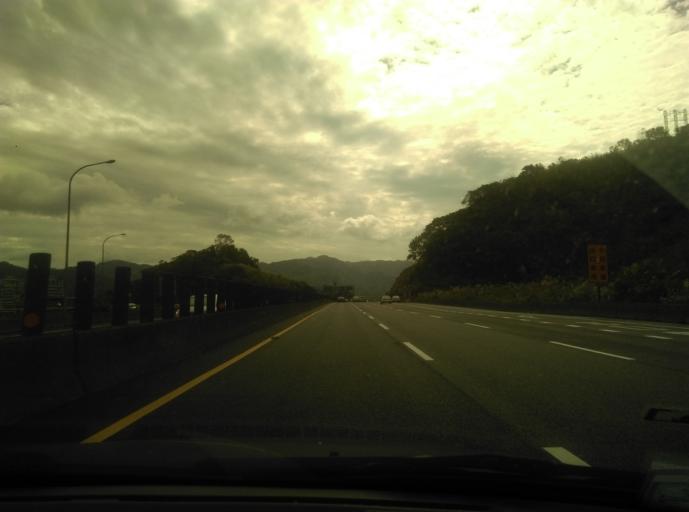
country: TW
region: Taiwan
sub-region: Keelung
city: Keelung
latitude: 25.0925
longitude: 121.6964
